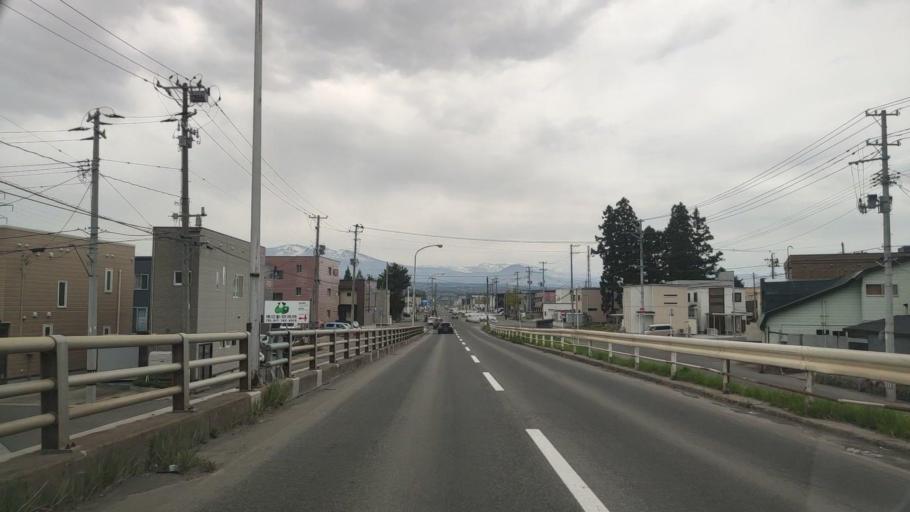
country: JP
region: Aomori
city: Aomori Shi
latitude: 40.8069
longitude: 140.7803
